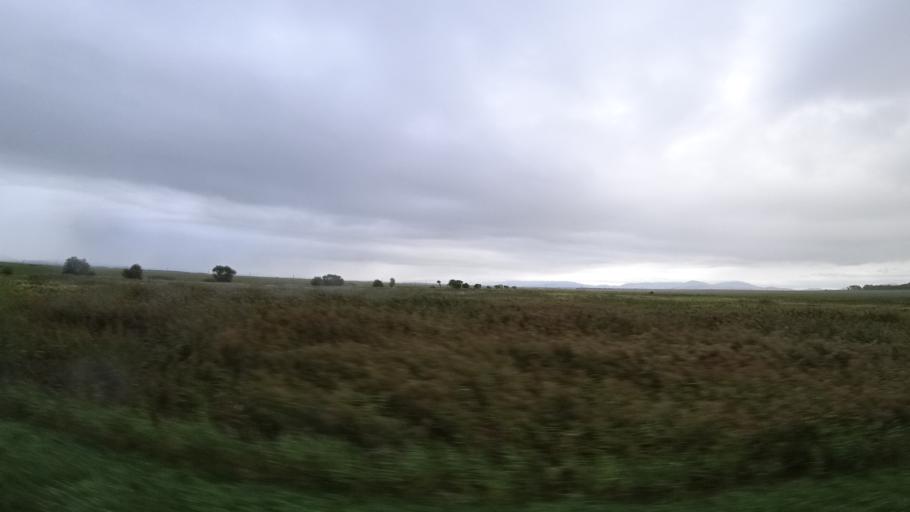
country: RU
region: Primorskiy
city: Chernigovka
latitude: 44.3809
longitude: 132.5296
